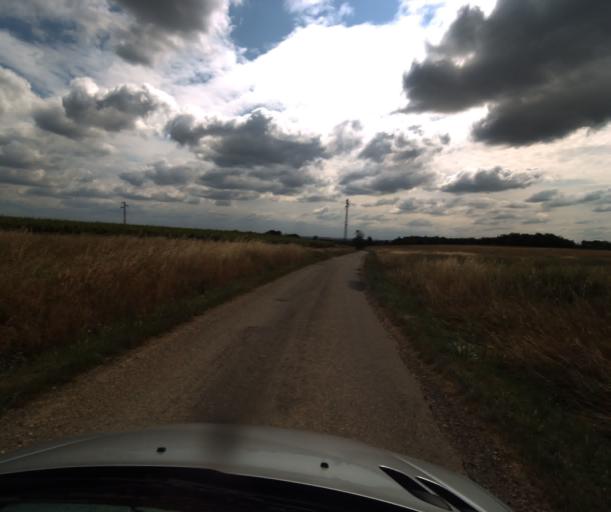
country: FR
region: Midi-Pyrenees
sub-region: Departement du Tarn-et-Garonne
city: Campsas
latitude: 43.9096
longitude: 1.3043
